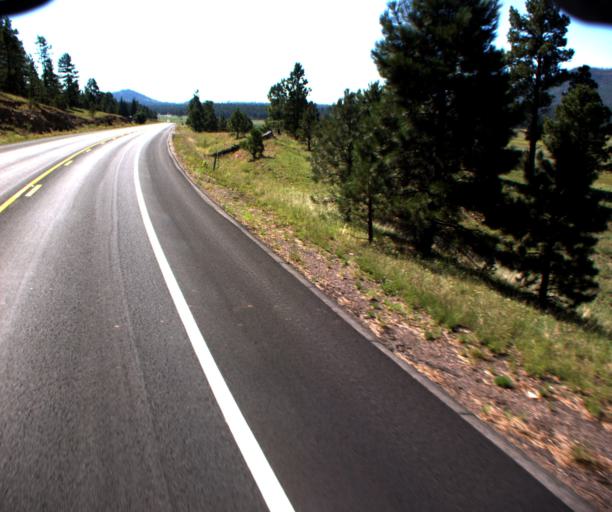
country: US
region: Arizona
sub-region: Apache County
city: Eagar
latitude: 33.8431
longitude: -109.1318
